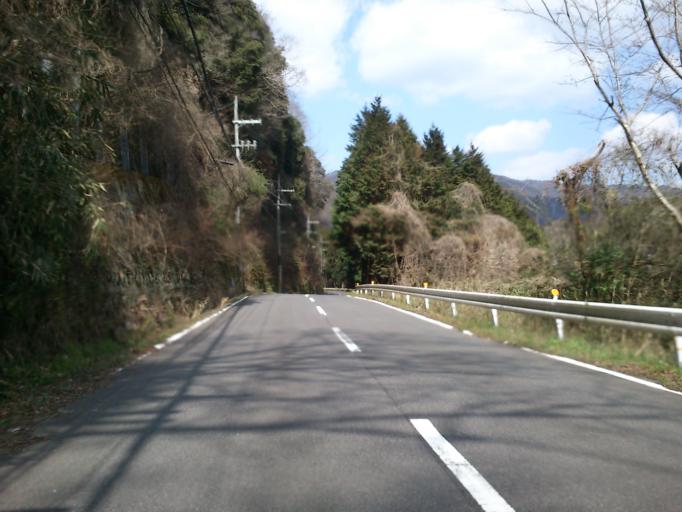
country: JP
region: Mie
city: Ueno-ebisumachi
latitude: 34.7664
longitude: 135.9932
